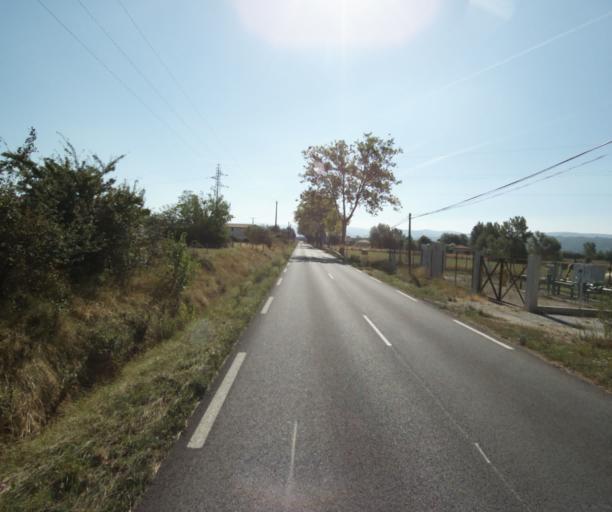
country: FR
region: Midi-Pyrenees
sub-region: Departement de la Haute-Garonne
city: Revel
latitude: 43.4666
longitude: 1.9796
